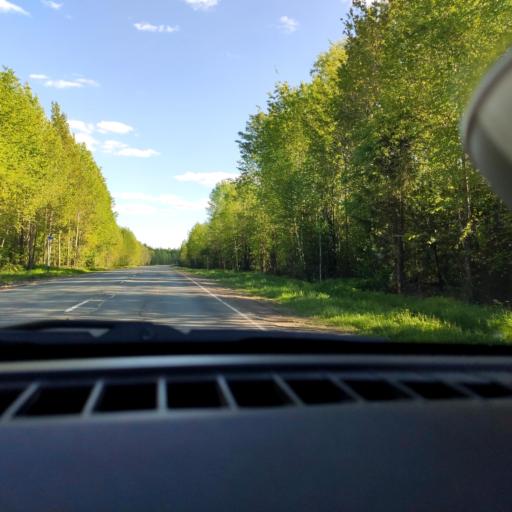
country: RU
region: Perm
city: Polazna
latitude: 58.2721
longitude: 56.1668
